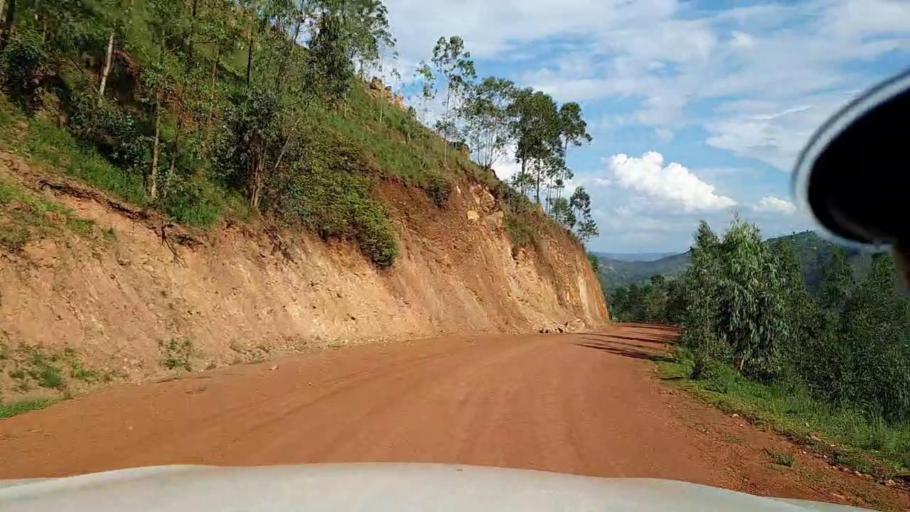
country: RW
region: Kigali
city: Kigali
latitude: -1.8477
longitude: 29.8636
